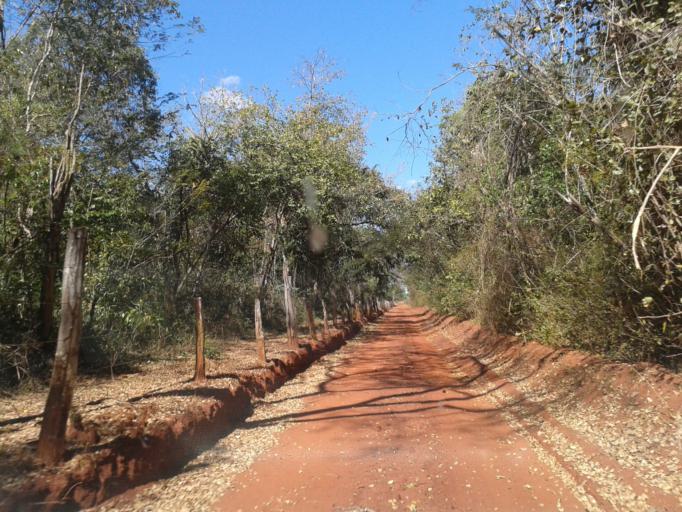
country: BR
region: Minas Gerais
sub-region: Santa Vitoria
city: Santa Vitoria
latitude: -19.0151
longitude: -50.4544
